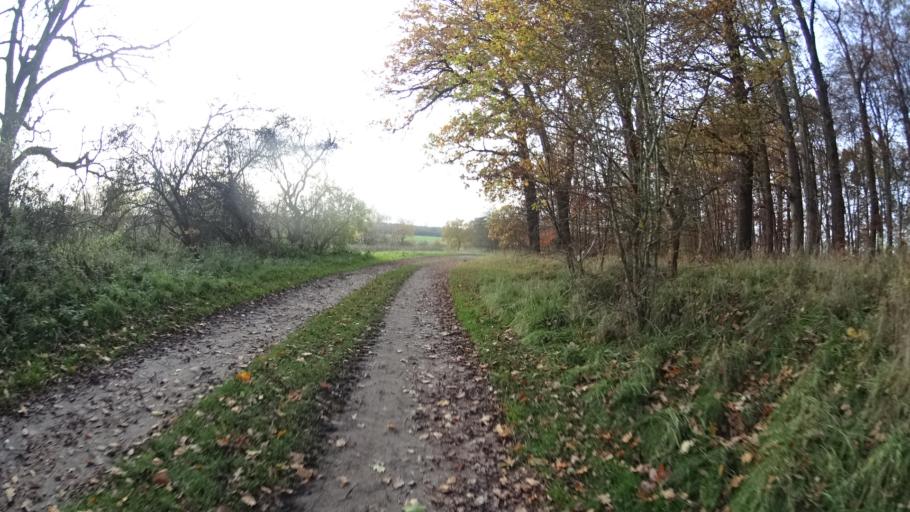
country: DE
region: Lower Saxony
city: Wendisch Evern
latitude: 53.2186
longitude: 10.4601
